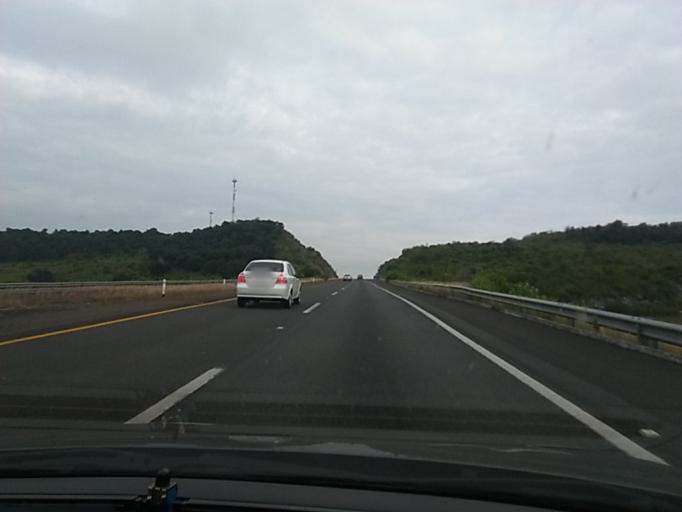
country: MX
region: Michoacan
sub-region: Puruandiro
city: San Lorenzo
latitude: 19.9438
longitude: -101.6328
